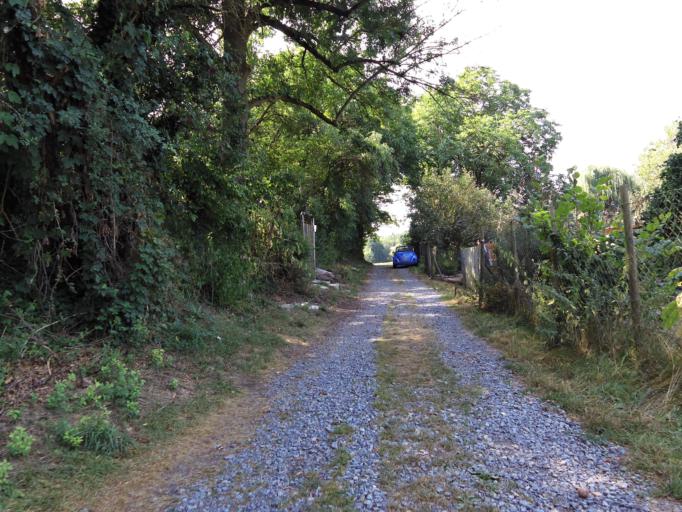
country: DE
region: Bavaria
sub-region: Regierungsbezirk Unterfranken
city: Estenfeld
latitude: 49.8242
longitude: 10.0085
